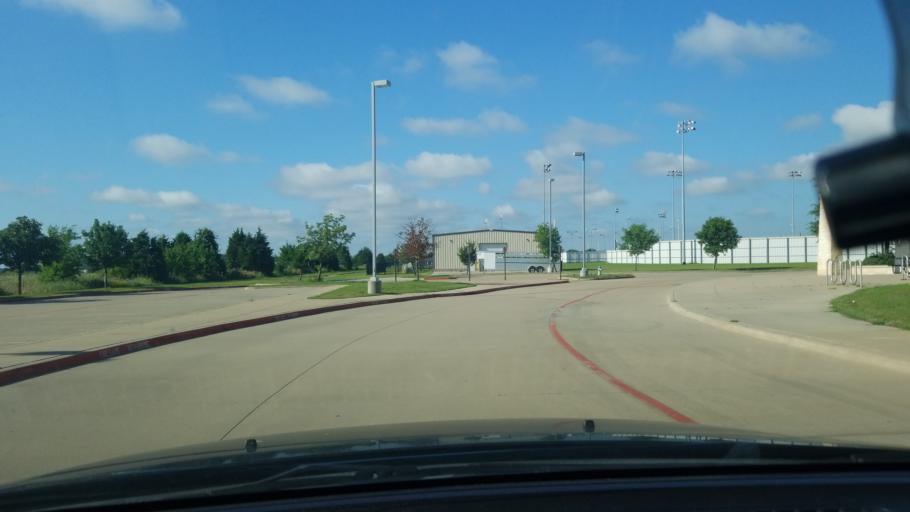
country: US
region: Texas
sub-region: Dallas County
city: Sunnyvale
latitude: 32.8017
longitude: -96.5560
